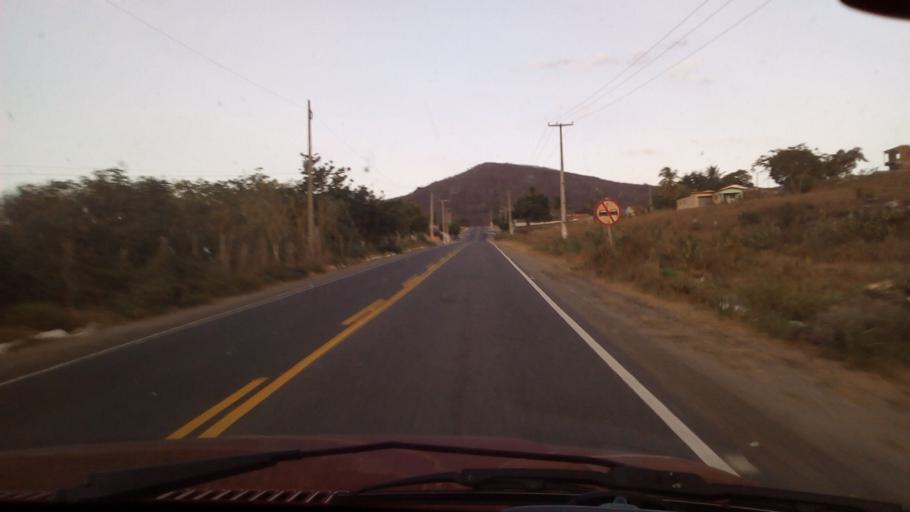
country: BR
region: Paraiba
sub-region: Belem
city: Belem
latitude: -6.7212
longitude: -35.5442
